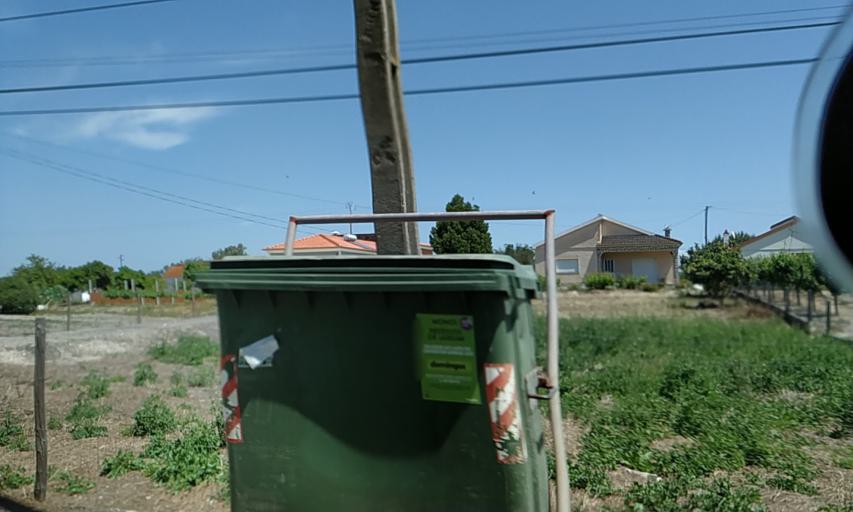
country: PT
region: Santarem
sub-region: Benavente
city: Poceirao
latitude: 38.6767
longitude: -8.7339
